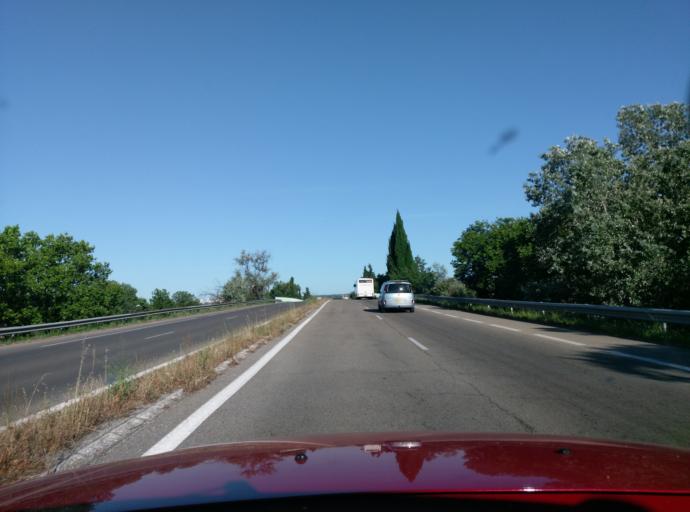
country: FR
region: Languedoc-Roussillon
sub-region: Departement du Gard
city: Rodilhan
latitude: 43.8351
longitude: 4.4086
